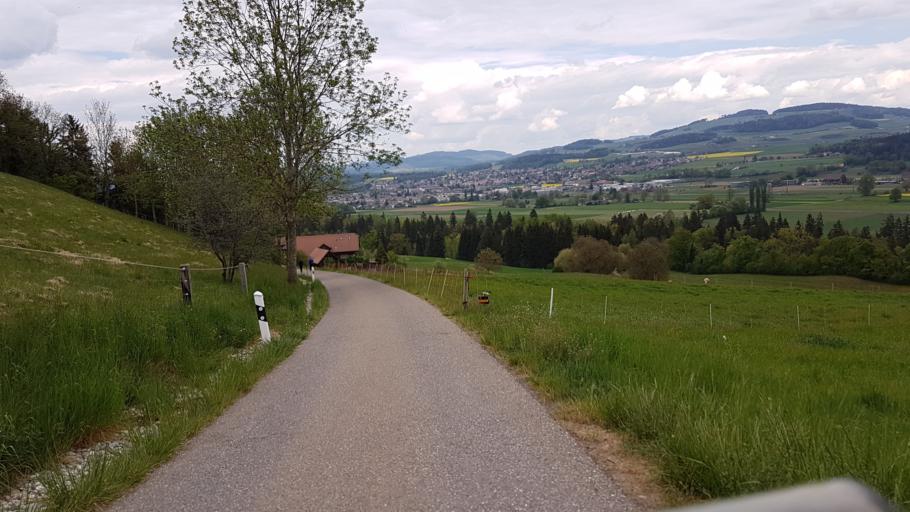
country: CH
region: Bern
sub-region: Bern-Mittelland District
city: Munsingen
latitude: 46.8506
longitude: 7.5519
